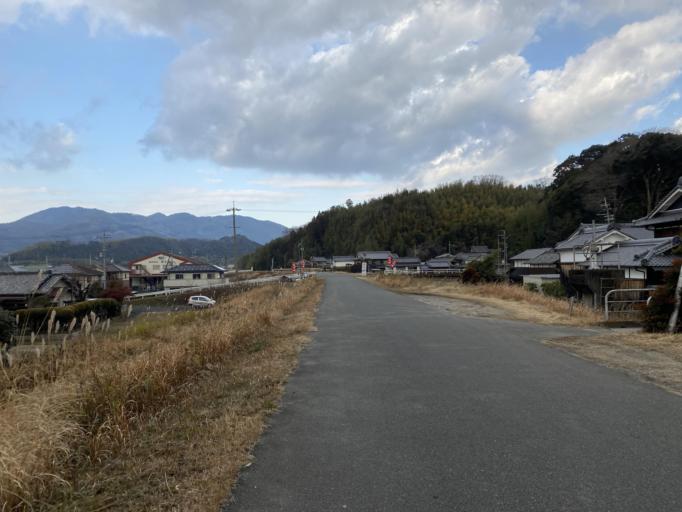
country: JP
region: Nara
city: Nara-shi
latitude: 34.7536
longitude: 135.8755
